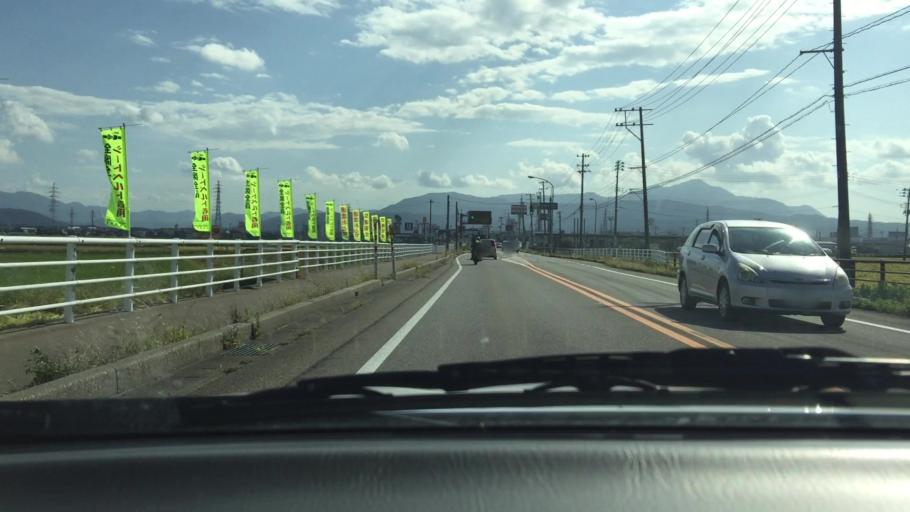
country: JP
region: Niigata
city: Kashiwazaki
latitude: 37.3841
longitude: 138.5835
